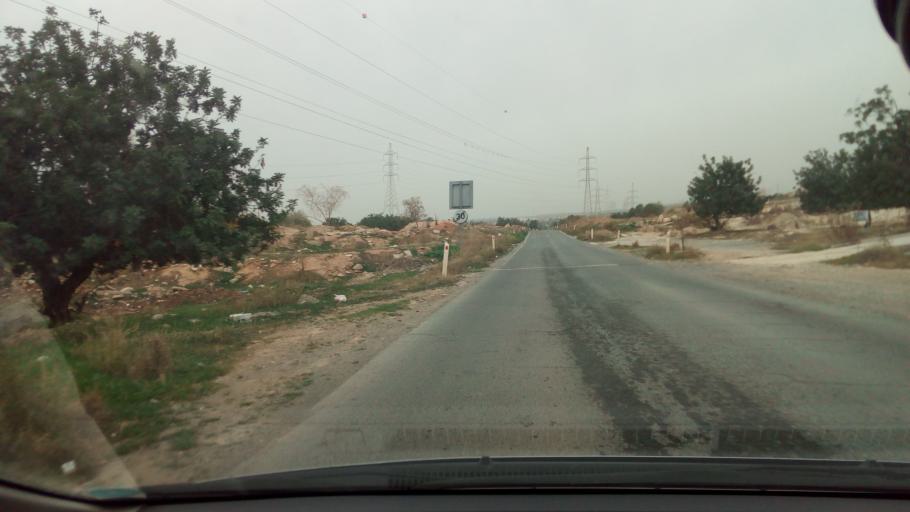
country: CY
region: Limassol
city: Pano Polemidia
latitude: 34.6962
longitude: 32.9840
